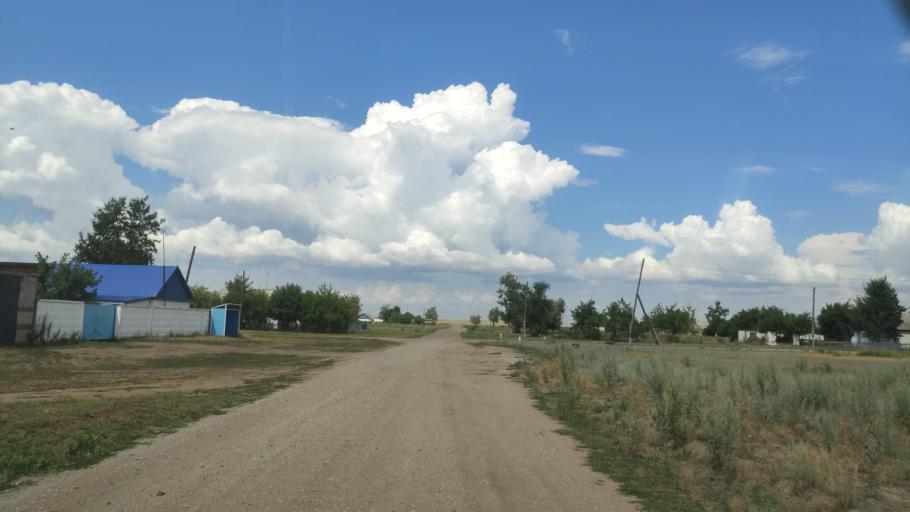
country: KZ
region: Pavlodar
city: Pavlodar
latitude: 52.6204
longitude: 77.2064
